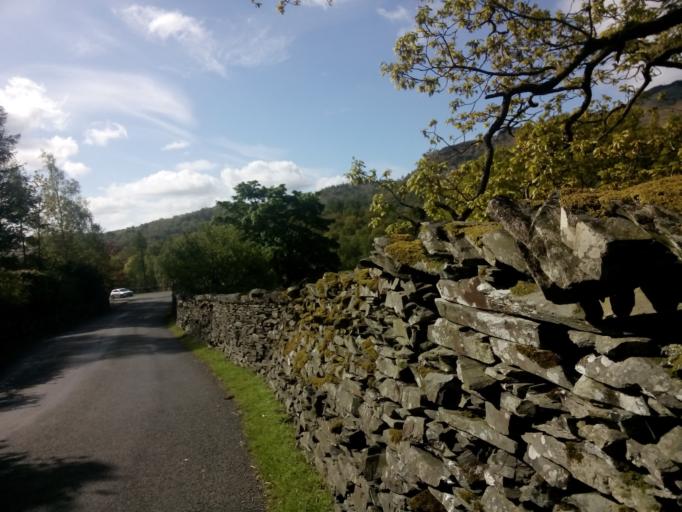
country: GB
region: England
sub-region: Cumbria
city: Ambleside
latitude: 54.4402
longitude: -3.0558
